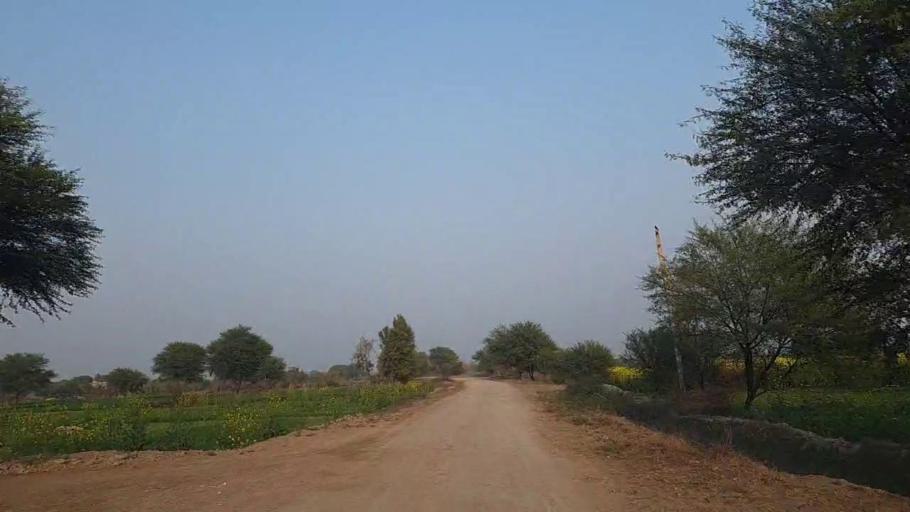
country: PK
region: Sindh
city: Nawabshah
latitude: 26.2527
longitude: 68.4748
